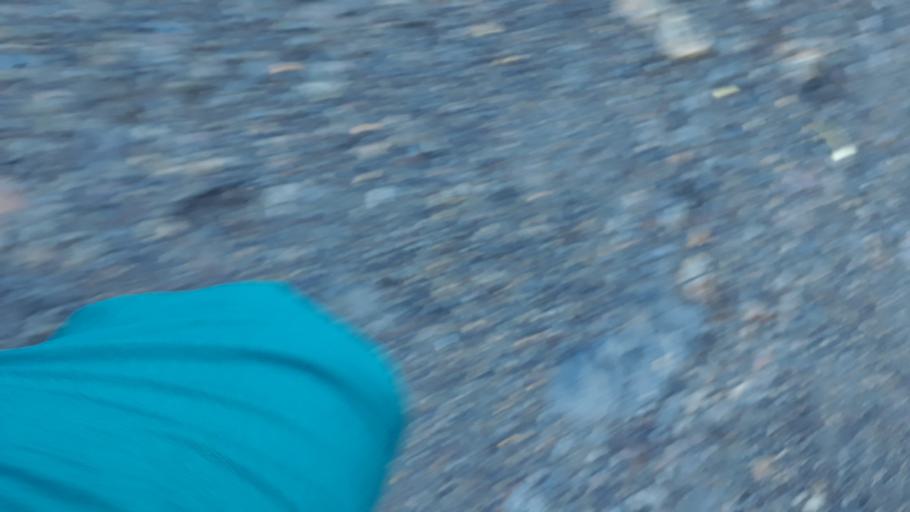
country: CO
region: Casanare
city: Nunchia
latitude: 5.6606
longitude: -72.4211
